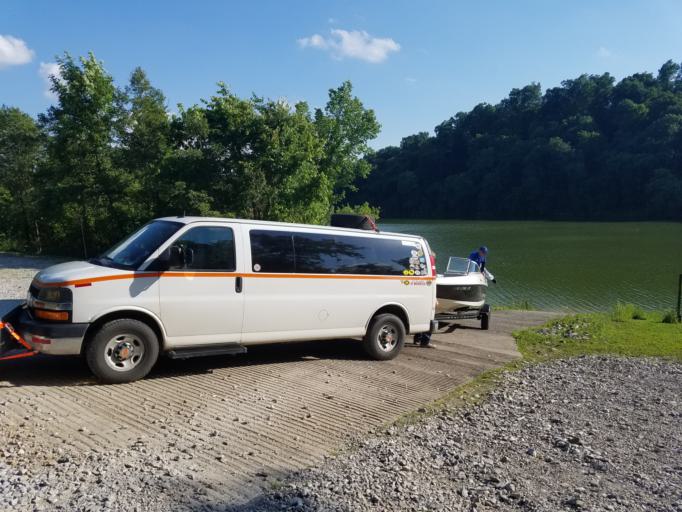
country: US
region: Kentucky
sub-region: Hart County
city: Munfordville
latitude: 37.3500
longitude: -86.0966
